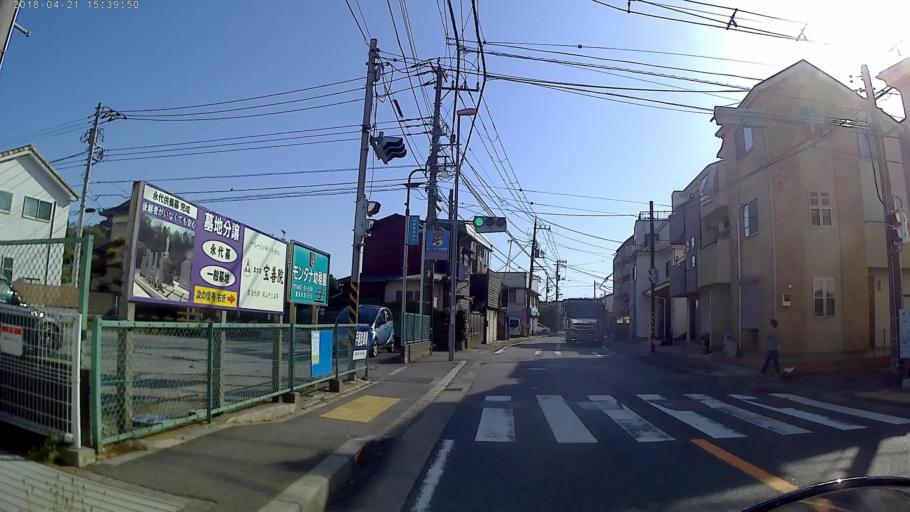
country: JP
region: Kanagawa
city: Fujisawa
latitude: 35.3133
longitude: 139.5004
